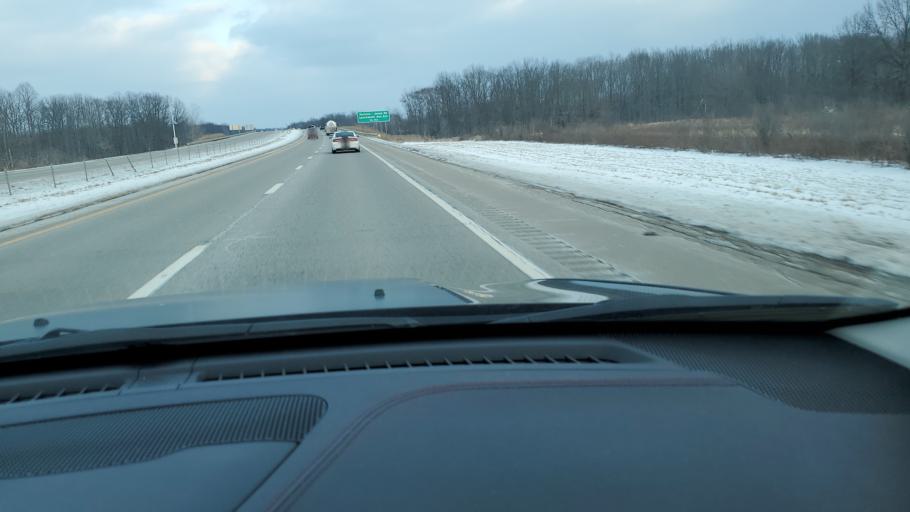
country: US
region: Ohio
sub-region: Trumbull County
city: Champion Heights
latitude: 41.2758
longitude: -80.8233
